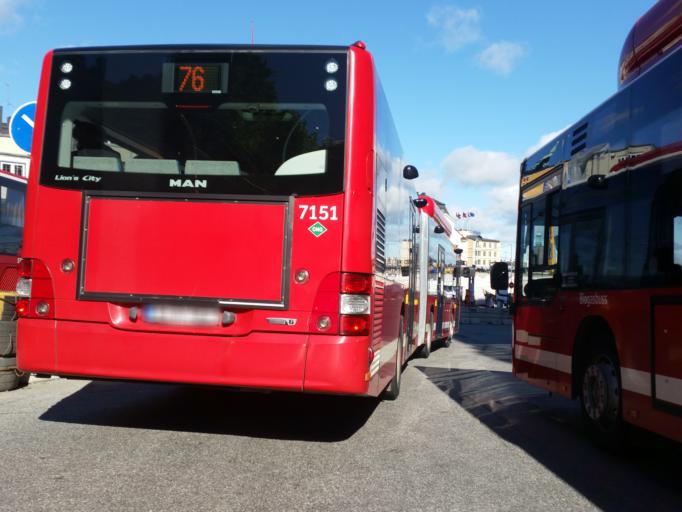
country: SE
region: Stockholm
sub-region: Stockholms Kommun
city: Stockholm
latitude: 59.3193
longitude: 18.0732
